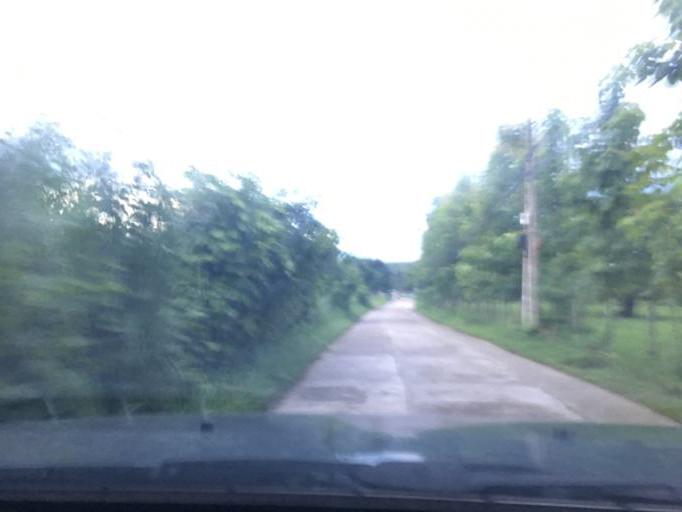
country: TH
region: Chiang Mai
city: San Sai
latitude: 18.8704
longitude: 98.9675
